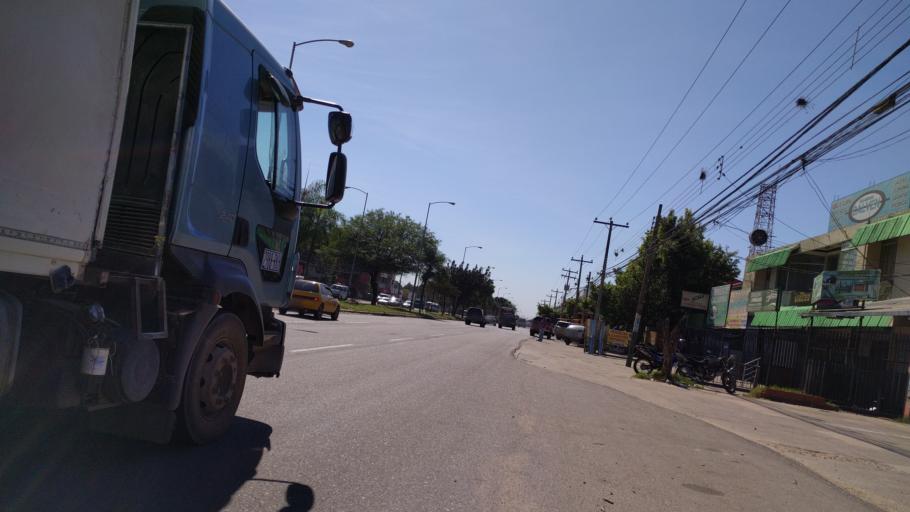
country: BO
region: Santa Cruz
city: Santa Cruz de la Sierra
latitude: -17.8209
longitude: -63.2183
